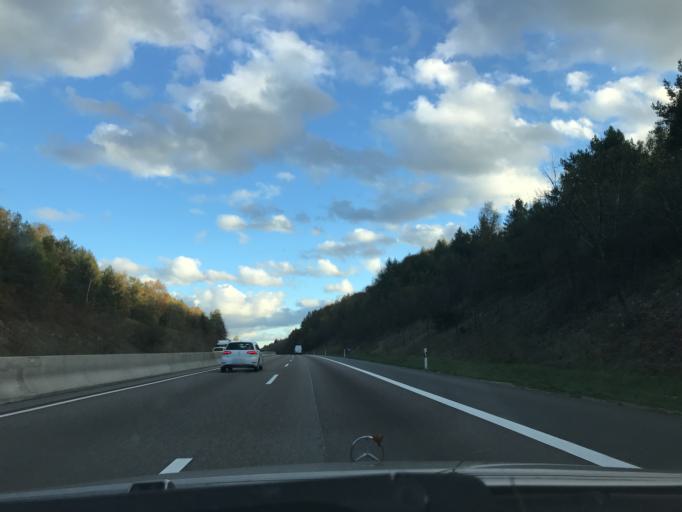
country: DE
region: North Rhine-Westphalia
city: Warburg
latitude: 51.4503
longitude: 9.1310
